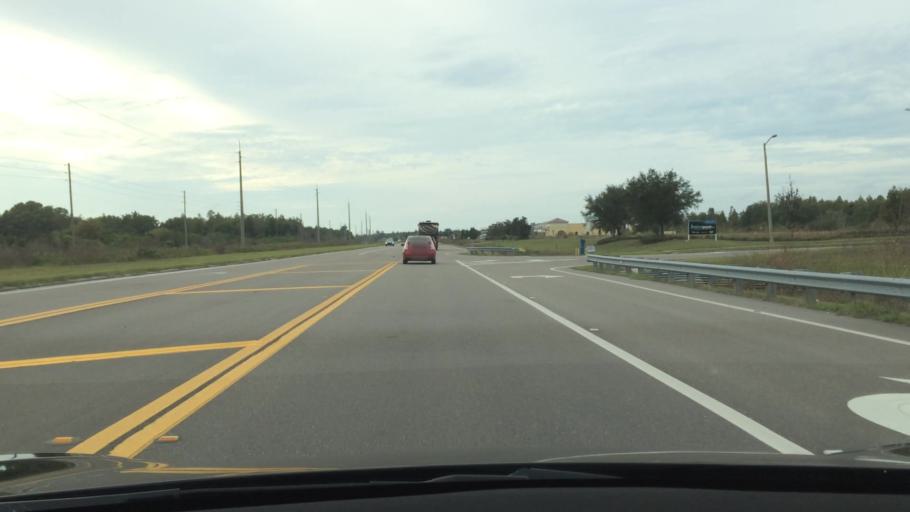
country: US
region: Florida
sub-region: Hillsborough County
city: Keystone
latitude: 28.1869
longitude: -82.6274
